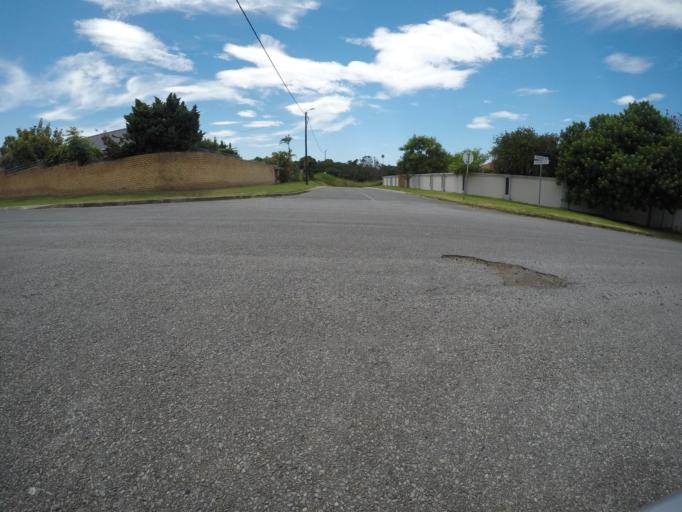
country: ZA
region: Eastern Cape
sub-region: Buffalo City Metropolitan Municipality
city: East London
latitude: -33.0422
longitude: 27.8520
